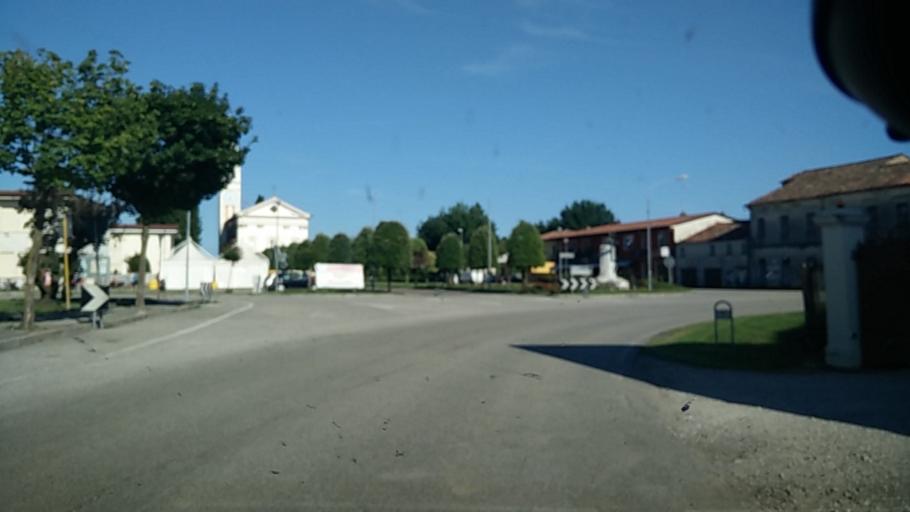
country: IT
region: Veneto
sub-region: Provincia di Treviso
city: Monastier di Treviso
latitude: 45.6786
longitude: 12.4035
